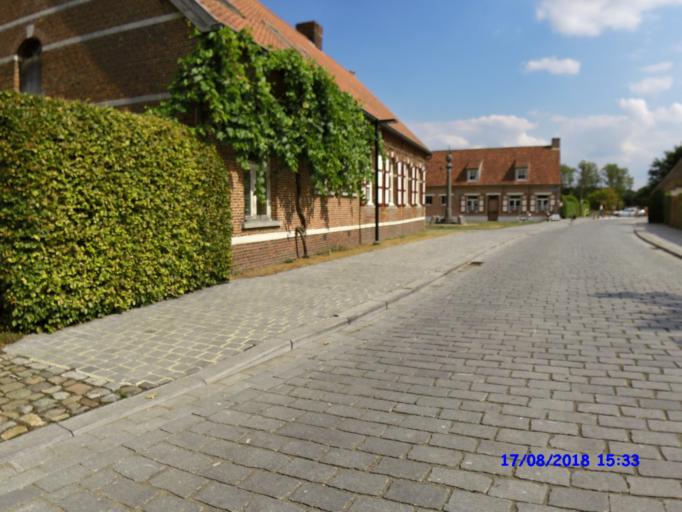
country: BE
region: Flanders
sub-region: Provincie Antwerpen
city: Berlaar
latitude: 51.1278
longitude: 4.6744
